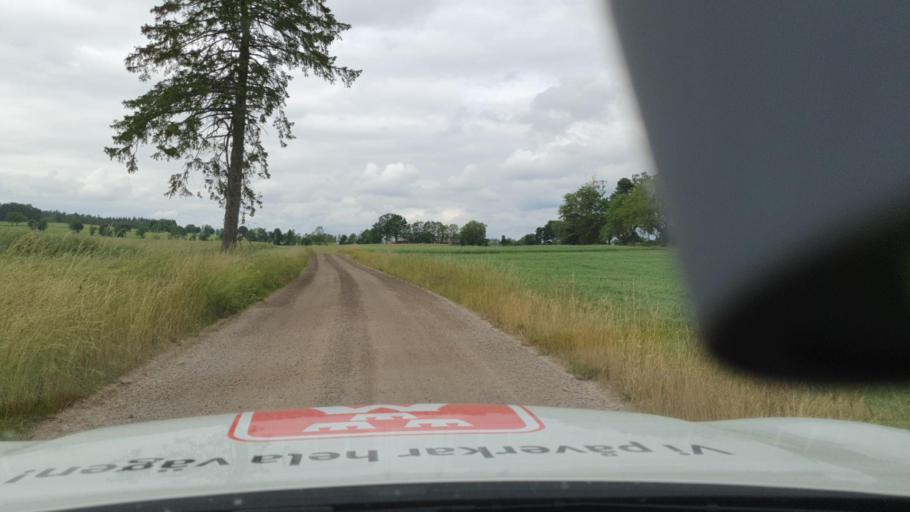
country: SE
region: Vaestra Goetaland
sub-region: Hjo Kommun
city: Hjo
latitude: 58.1906
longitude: 14.1757
